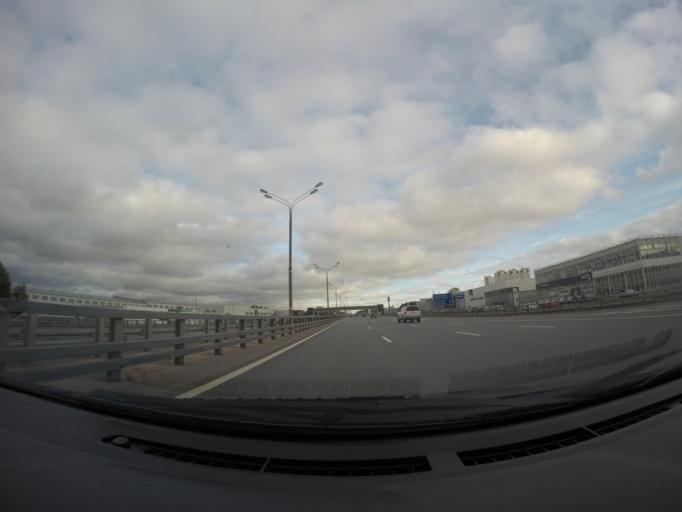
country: RU
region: Moskovskaya
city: Krasnoznamensk
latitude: 55.6047
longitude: 37.0184
